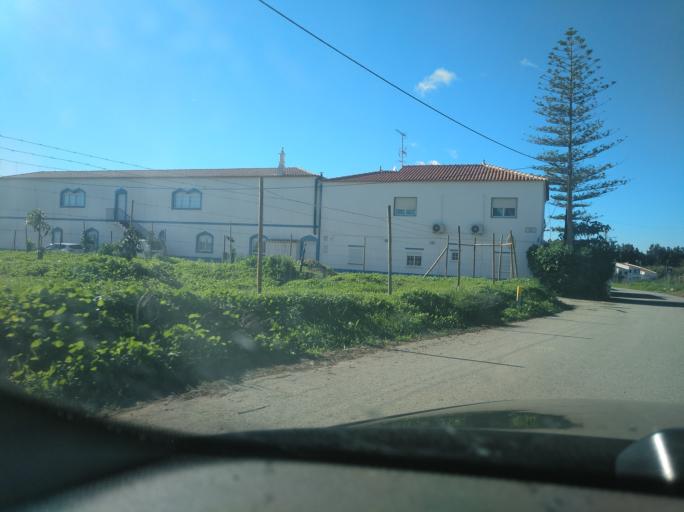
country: PT
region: Faro
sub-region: Tavira
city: Tavira
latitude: 37.1591
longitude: -7.5573
